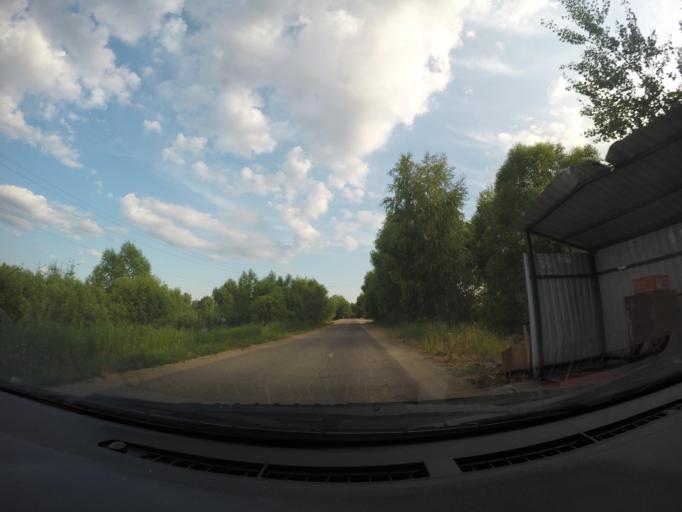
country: RU
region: Moskovskaya
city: Krasnyy Tkach
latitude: 55.4257
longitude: 39.2435
